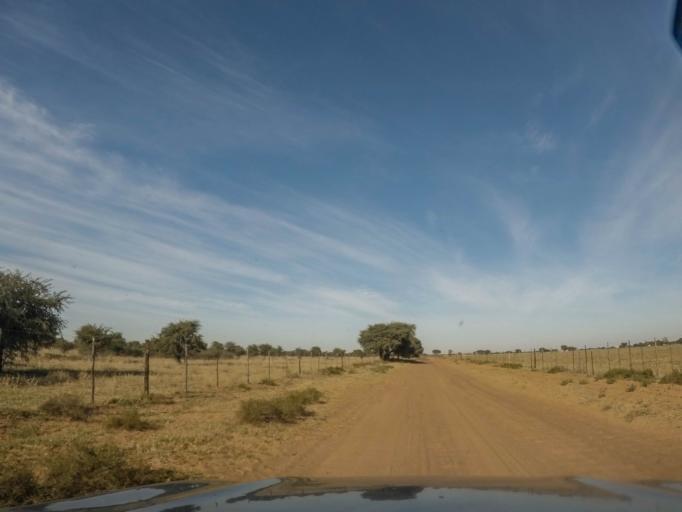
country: BW
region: South East
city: Janeng
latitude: -25.6542
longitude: 25.2527
